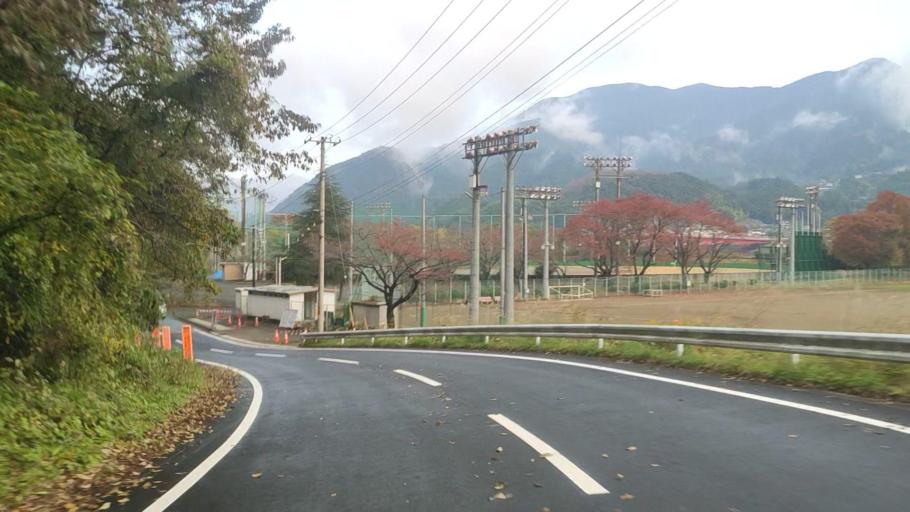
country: JP
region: Shizuoka
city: Fujinomiya
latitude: 35.2761
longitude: 138.4573
